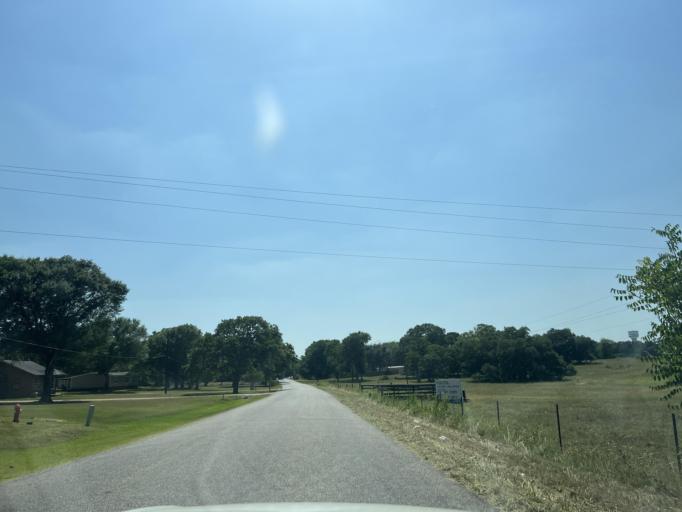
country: US
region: Texas
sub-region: Washington County
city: Brenham
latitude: 30.1620
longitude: -96.4245
